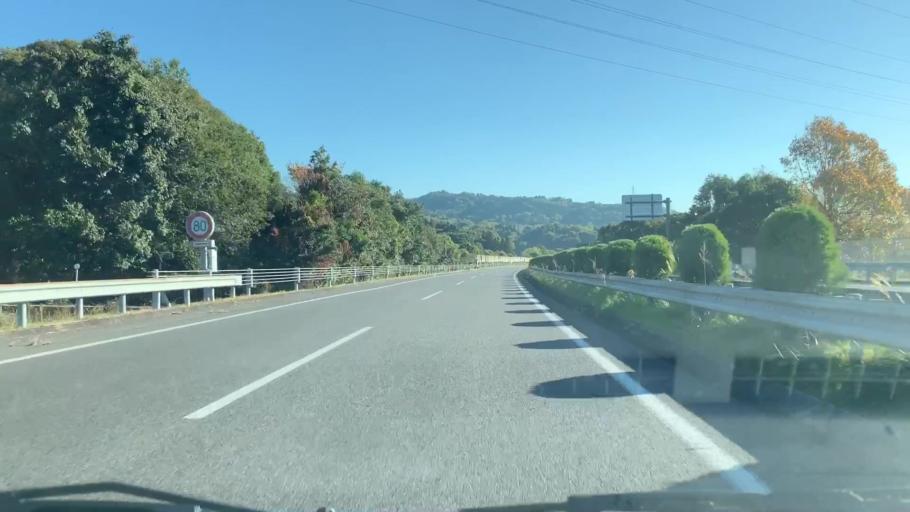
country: JP
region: Saga Prefecture
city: Takeocho-takeo
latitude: 33.2883
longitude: 130.1338
